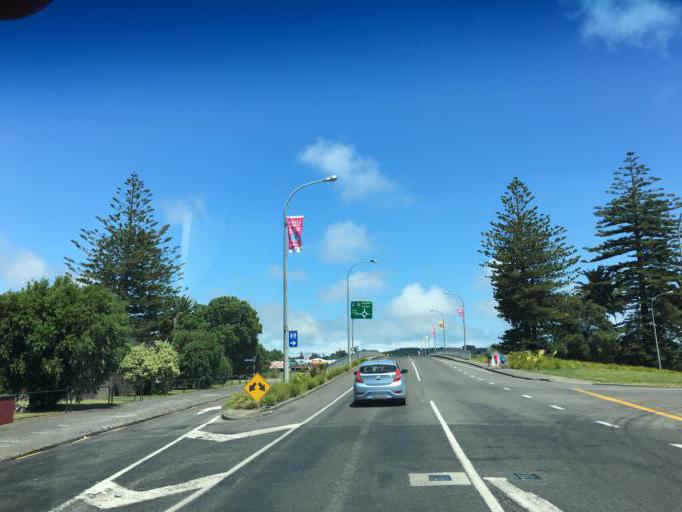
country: NZ
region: Hawke's Bay
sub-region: Wairoa District
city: Wairoa
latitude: -39.0300
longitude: 177.4191
